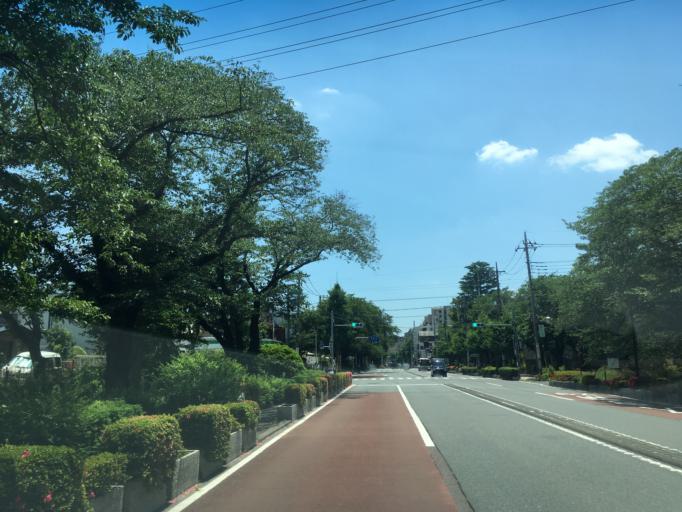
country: JP
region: Tokyo
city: Kokubunji
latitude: 35.6876
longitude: 139.4472
